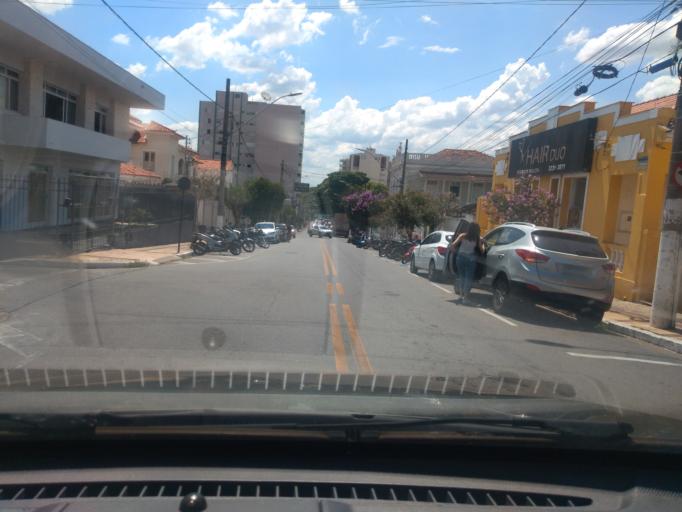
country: BR
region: Minas Gerais
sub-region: Tres Coracoes
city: Tres Coracoes
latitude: -21.6990
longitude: -45.2535
